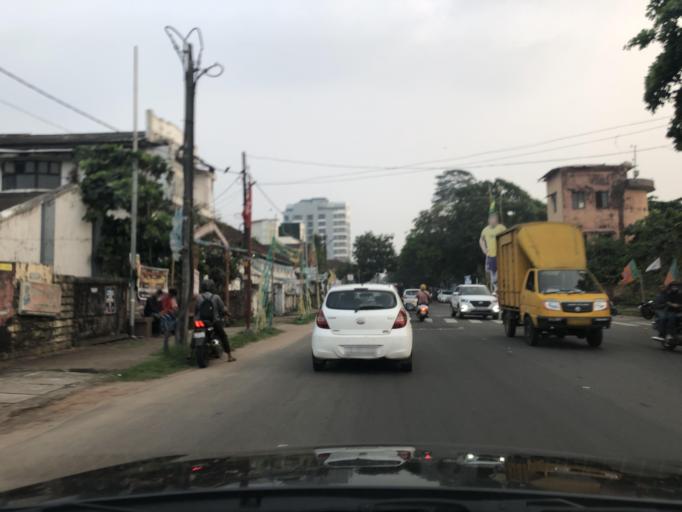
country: IN
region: Kerala
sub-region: Kozhikode
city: Kozhikode
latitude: 11.2628
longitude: 75.7681
